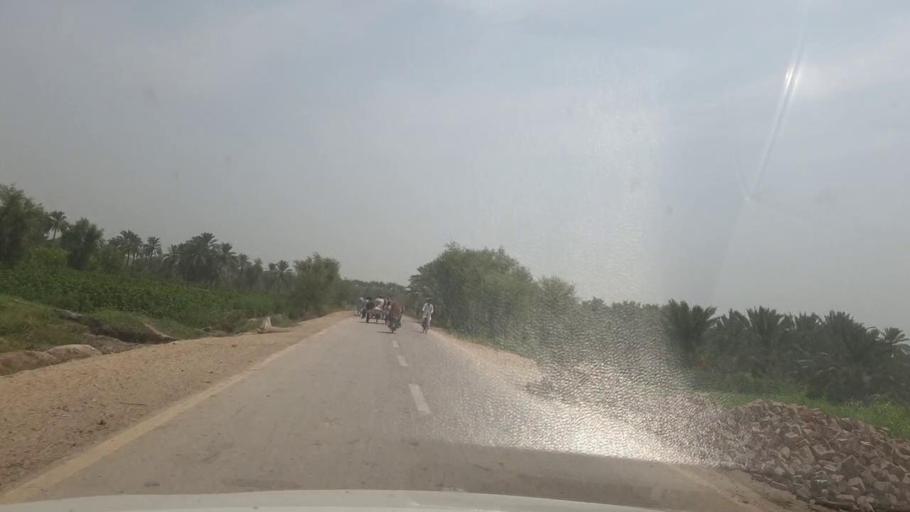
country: PK
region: Sindh
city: Kot Diji
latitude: 27.3876
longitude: 68.6569
